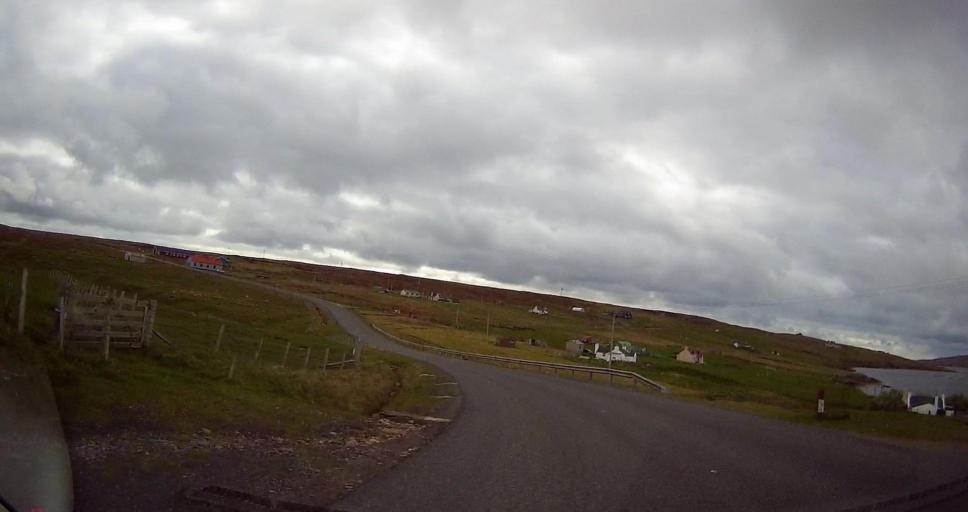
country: GB
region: Scotland
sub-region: Shetland Islands
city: Shetland
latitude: 60.6619
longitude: -1.0509
